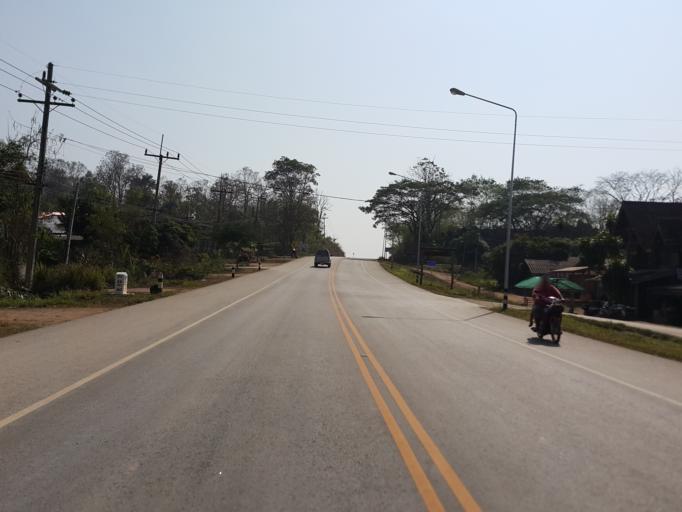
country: TH
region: Lampang
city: Mueang Pan
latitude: 18.9054
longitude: 99.6063
